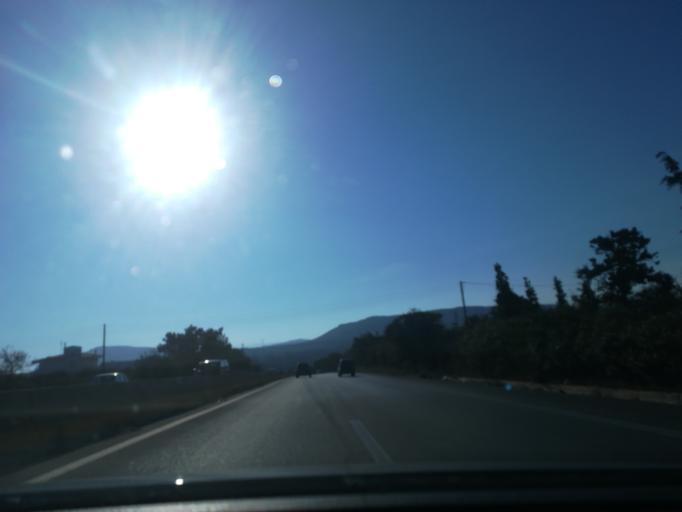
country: GR
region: Crete
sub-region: Nomos Irakleiou
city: Gournes
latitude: 35.3265
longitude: 25.2742
